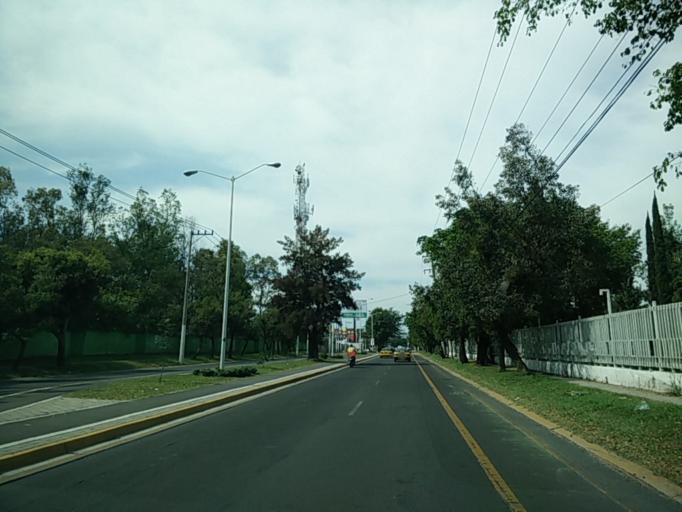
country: MX
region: Jalisco
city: Nuevo Mexico
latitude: 20.7308
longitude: -103.4483
